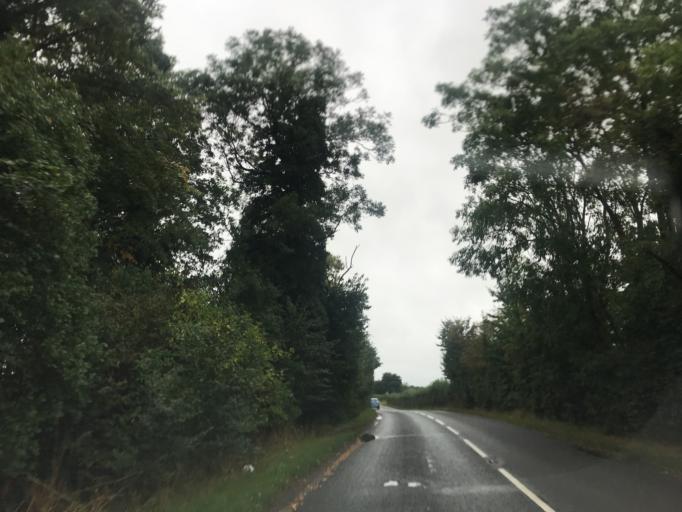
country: GB
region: England
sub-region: Buckinghamshire
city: Stone
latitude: 51.8008
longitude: -0.8500
